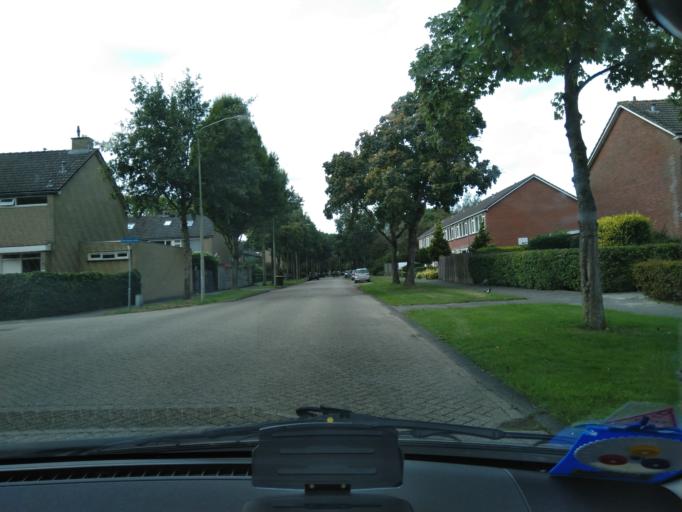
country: NL
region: Drenthe
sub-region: Gemeente Assen
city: Assen
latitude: 53.0065
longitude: 6.5397
